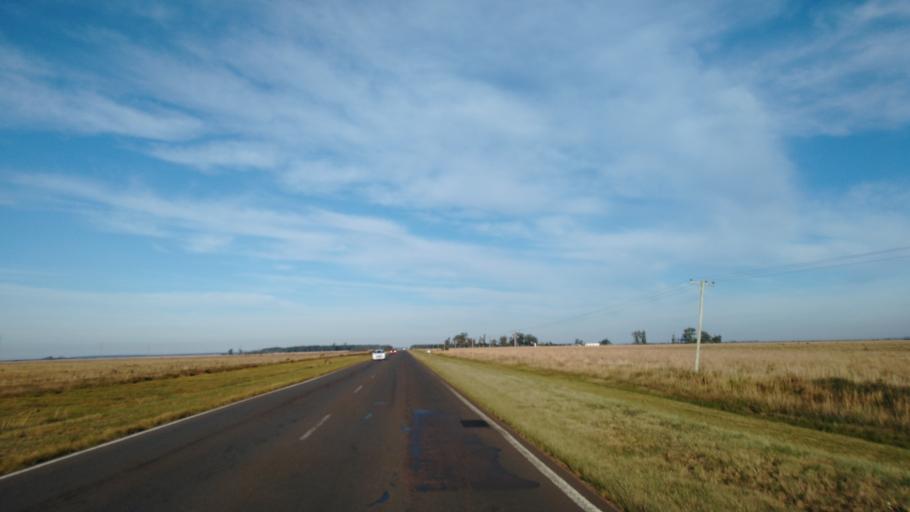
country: AR
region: Corrientes
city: La Cruz
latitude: -29.2316
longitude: -56.7217
